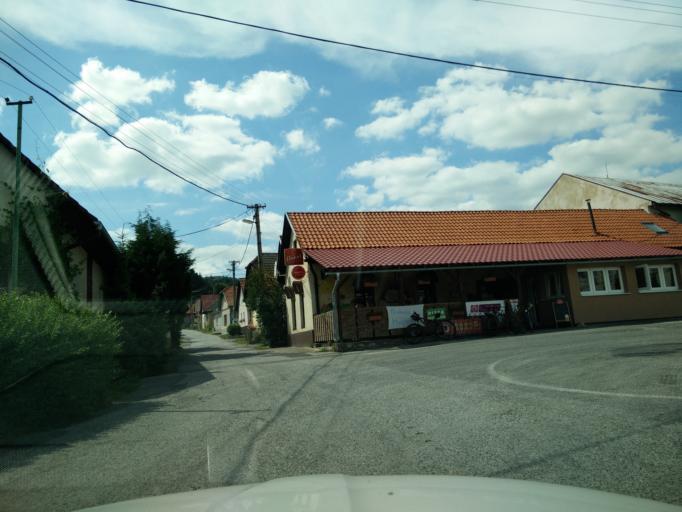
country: SK
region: Nitriansky
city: Bojnice
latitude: 48.8338
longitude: 18.5884
